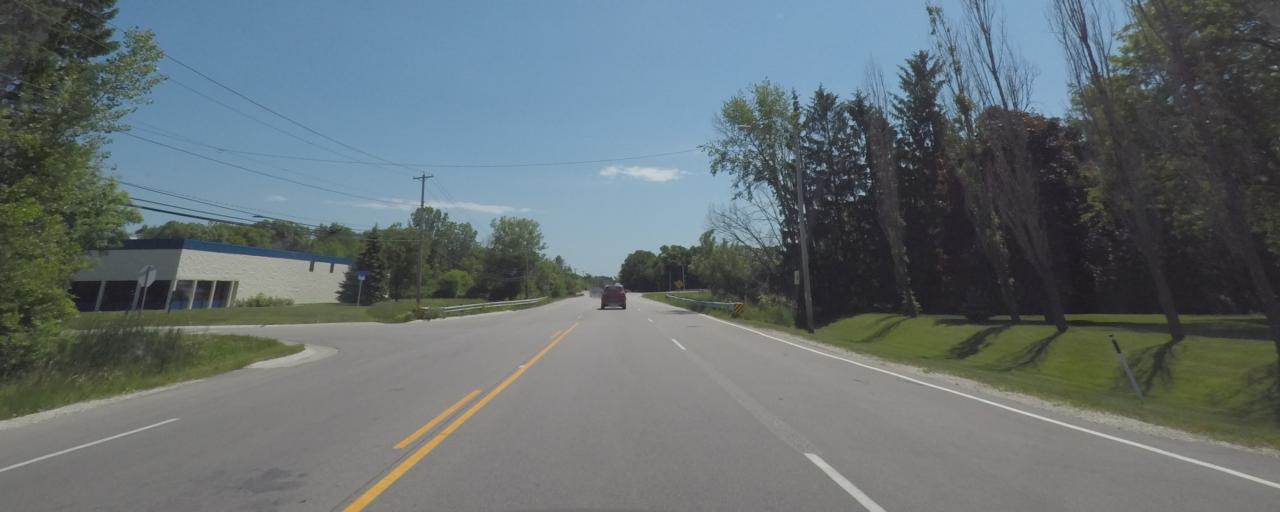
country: US
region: Wisconsin
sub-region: Waukesha County
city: New Berlin
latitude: 42.9871
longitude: -88.1282
